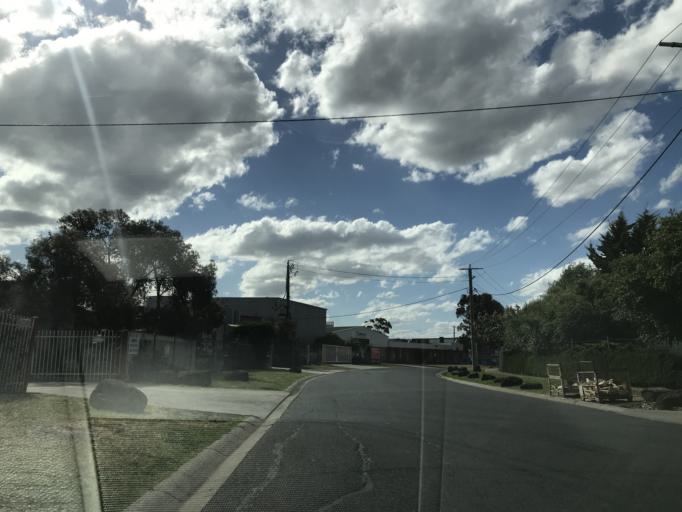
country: AU
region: Victoria
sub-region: Brimbank
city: Sunshine West
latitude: -37.8119
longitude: 144.8132
